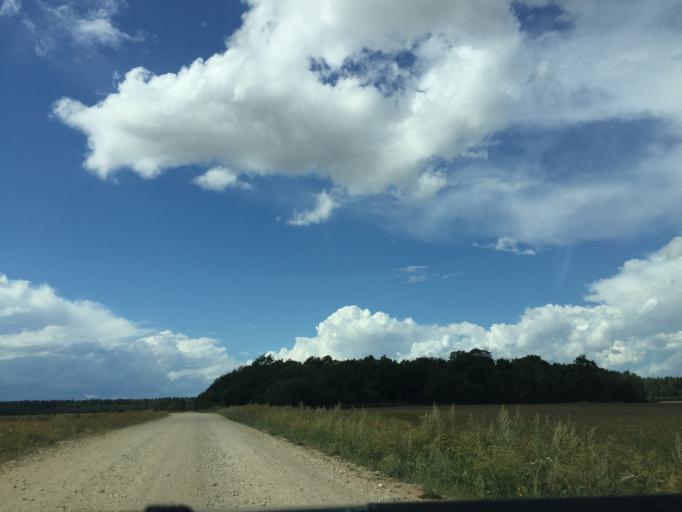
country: LT
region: Siauliu apskritis
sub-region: Joniskis
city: Joniskis
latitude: 56.3426
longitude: 23.6136
